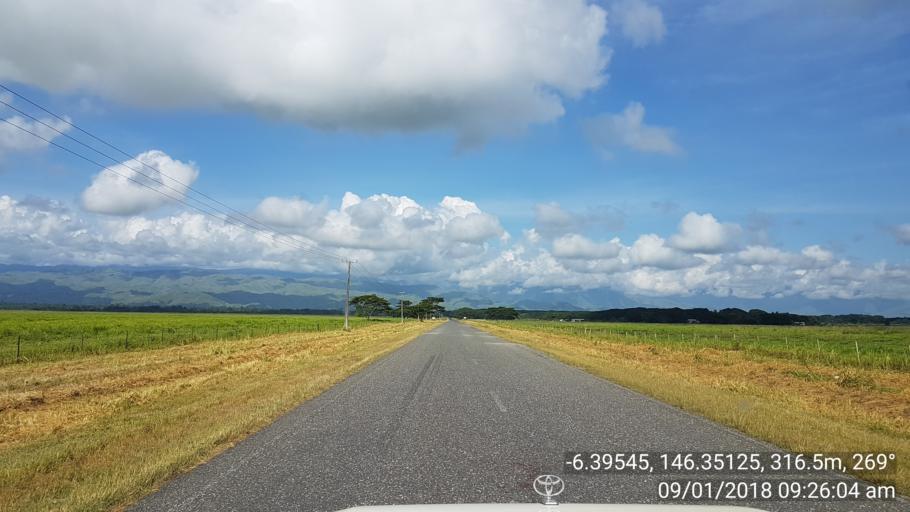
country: PG
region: Eastern Highlands
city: Kainantu
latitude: -6.3956
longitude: 146.3511
